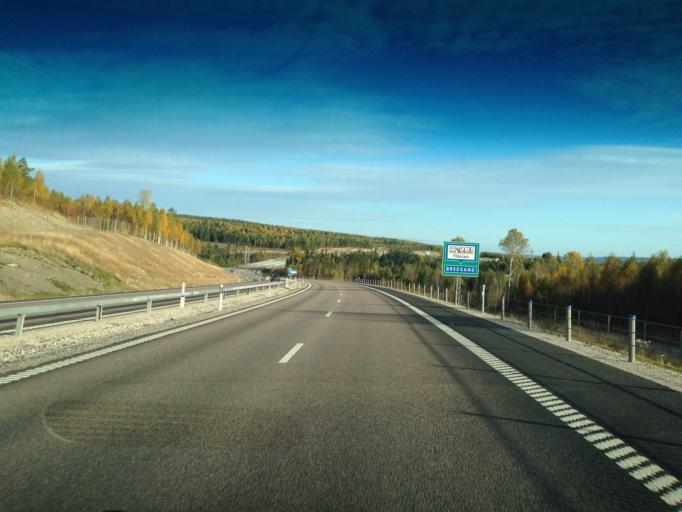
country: SE
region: Vaesternorrland
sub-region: Sundsvalls Kommun
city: Stockvik
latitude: 62.3277
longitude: 17.3458
